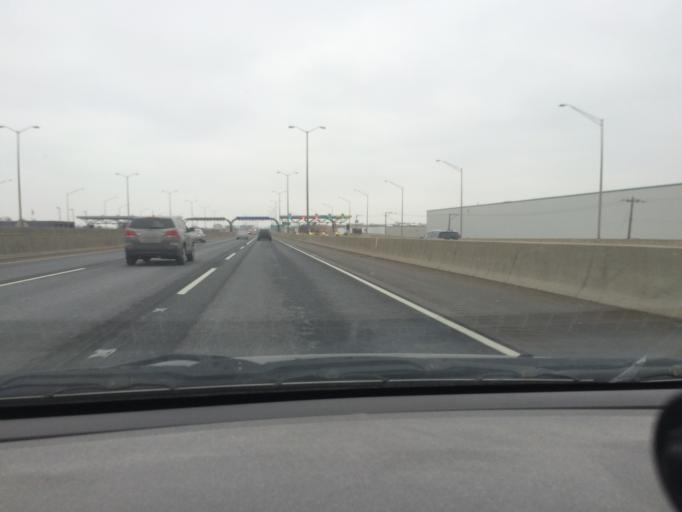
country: US
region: Illinois
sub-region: DuPage County
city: Glendale Heights
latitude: 41.9210
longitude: -88.0377
